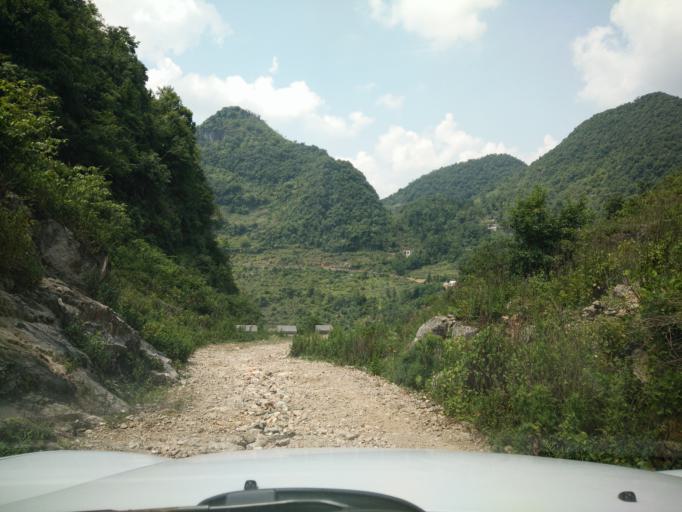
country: CN
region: Guangxi Zhuangzu Zizhiqu
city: Xinzhou
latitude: 25.0230
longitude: 105.7053
